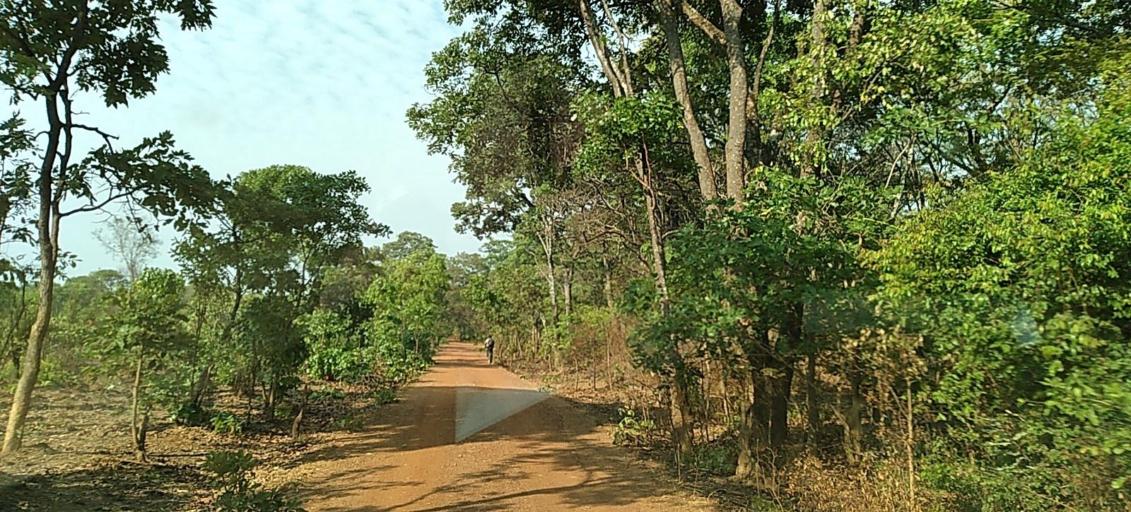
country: ZM
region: Copperbelt
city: Kalulushi
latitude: -12.9937
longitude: 27.7137
